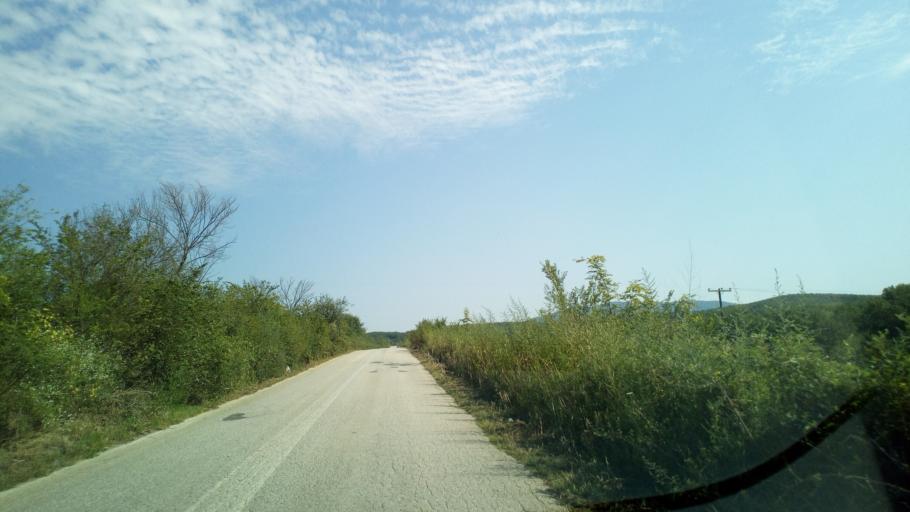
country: GR
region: Central Macedonia
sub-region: Nomos Thessalonikis
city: Askos
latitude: 40.7656
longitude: 23.3768
